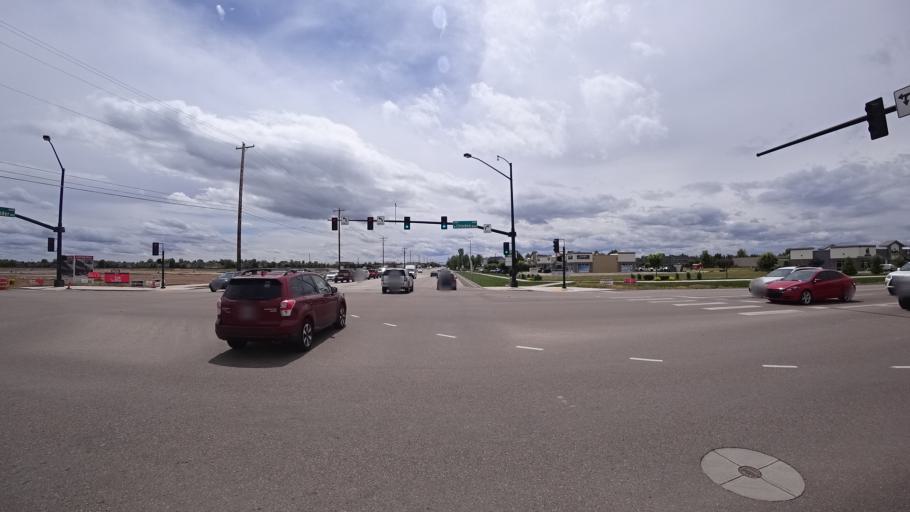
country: US
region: Idaho
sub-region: Ada County
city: Meridian
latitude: 43.6631
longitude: -116.4139
